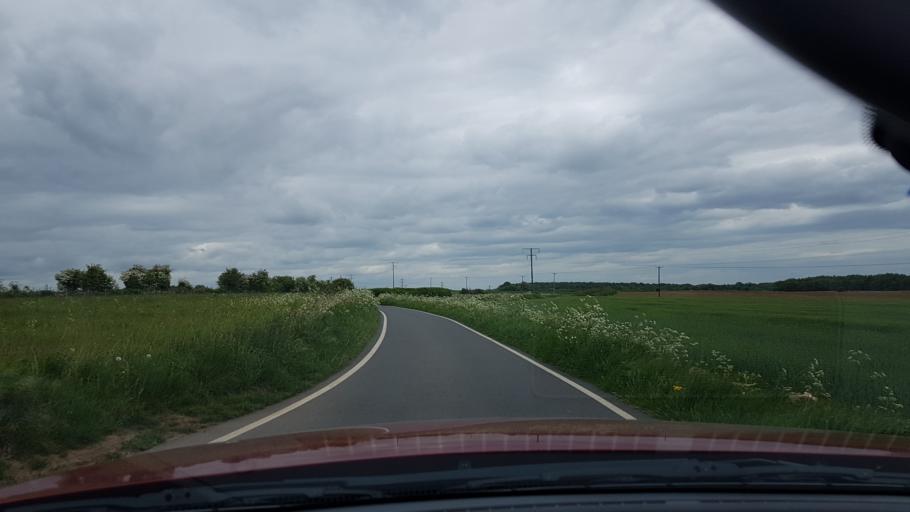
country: GB
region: England
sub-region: Rotherham
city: Maltby
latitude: 53.3995
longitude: -1.2028
